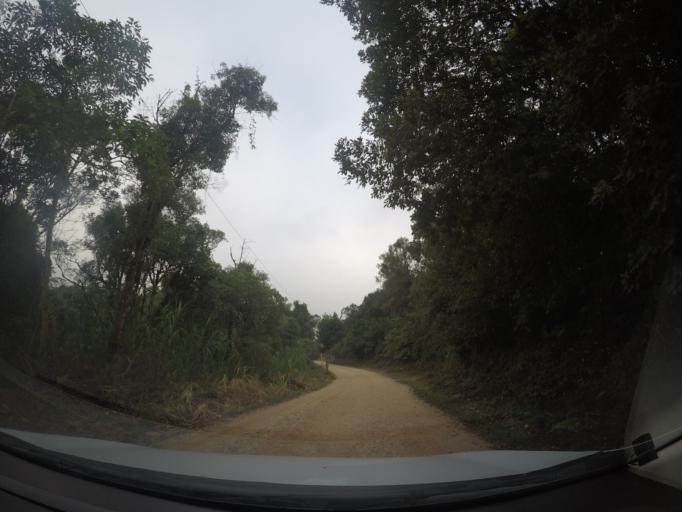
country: BR
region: Parana
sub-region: Colombo
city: Colombo
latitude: -25.3161
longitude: -49.2471
